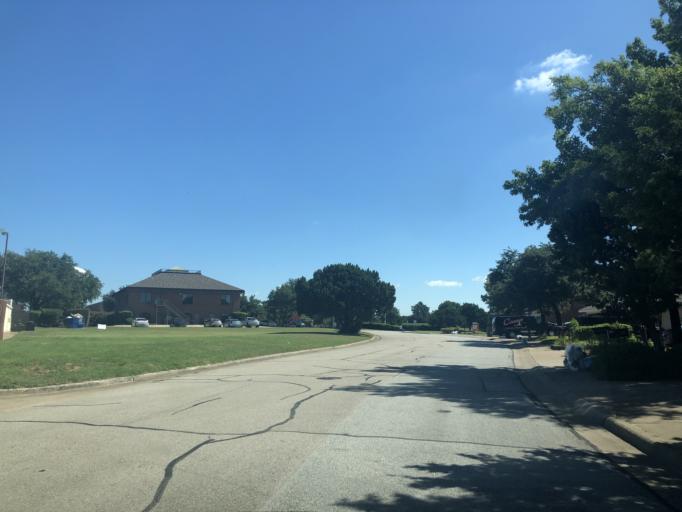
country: US
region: Texas
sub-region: Dallas County
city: Duncanville
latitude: 32.6445
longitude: -96.9422
